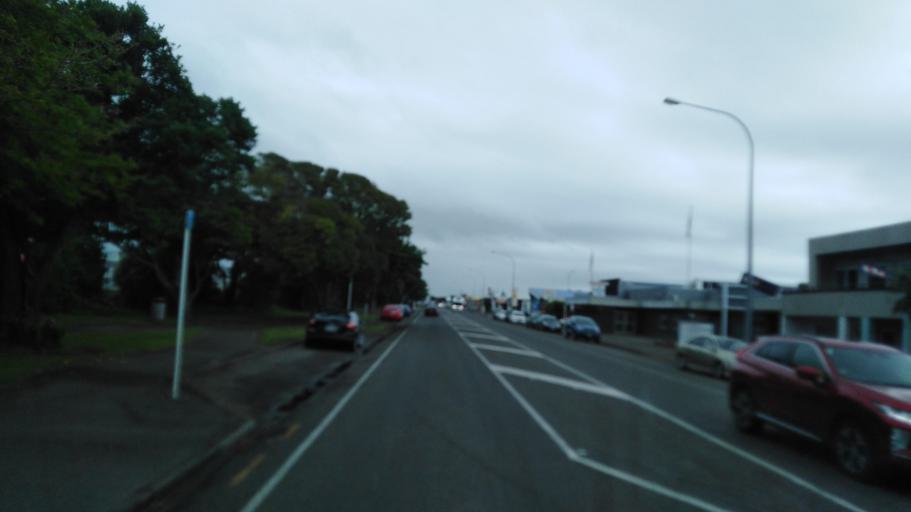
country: NZ
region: Manawatu-Wanganui
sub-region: Horowhenua District
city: Levin
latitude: -40.6300
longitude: 175.2788
